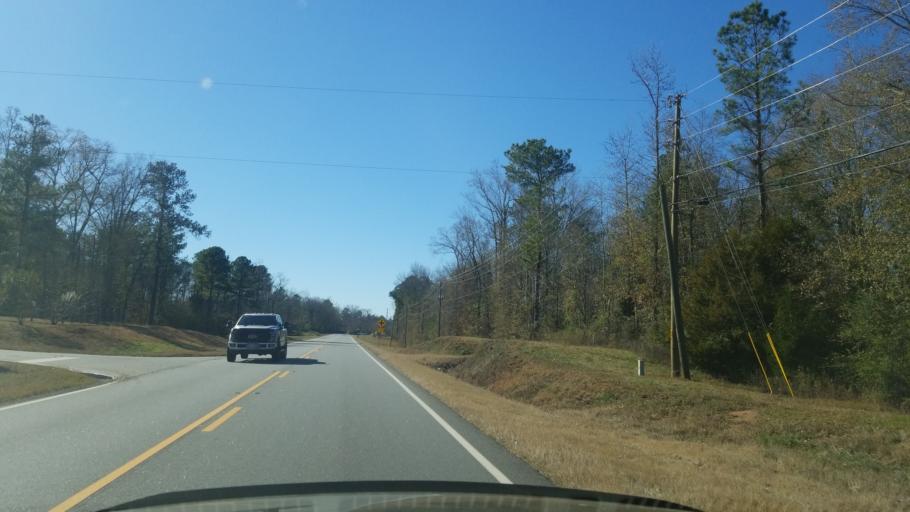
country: US
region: Georgia
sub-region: Harris County
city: Hamilton
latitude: 32.6307
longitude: -84.7663
